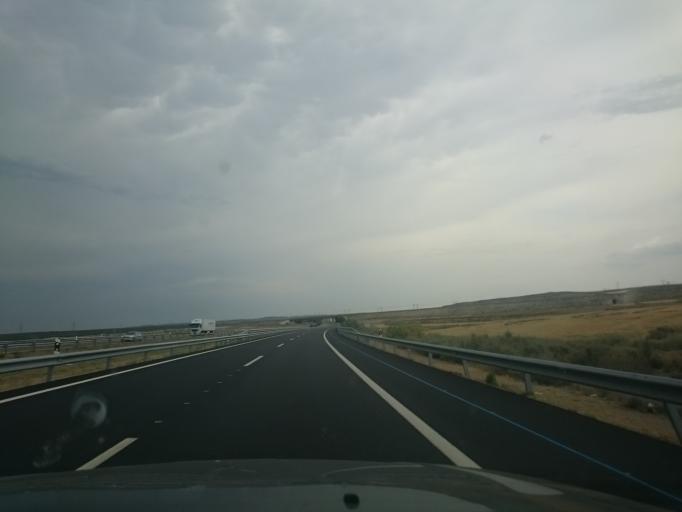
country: ES
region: Aragon
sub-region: Provincia de Zaragoza
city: Pina de Ebro
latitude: 41.5271
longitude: -0.5035
